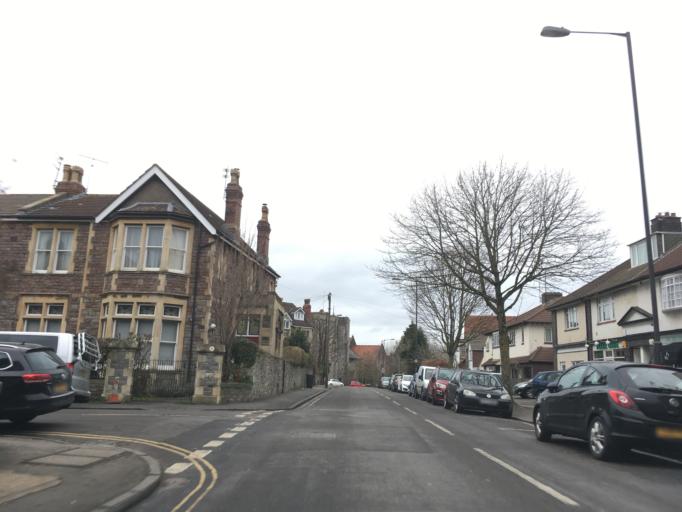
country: GB
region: England
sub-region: Bristol
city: Bristol
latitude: 51.4748
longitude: -2.6107
